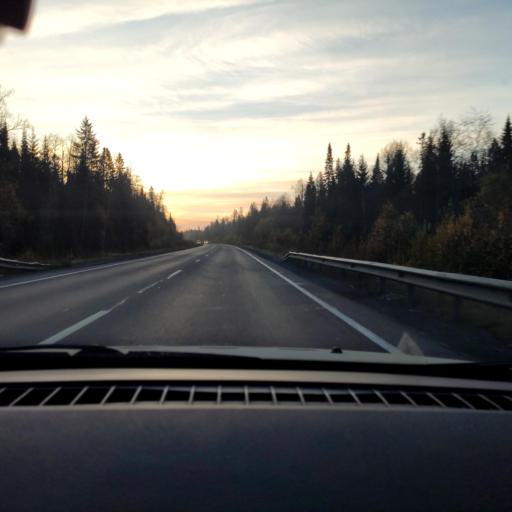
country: RU
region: Perm
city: Novyye Lyady
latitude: 58.0306
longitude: 56.4875
